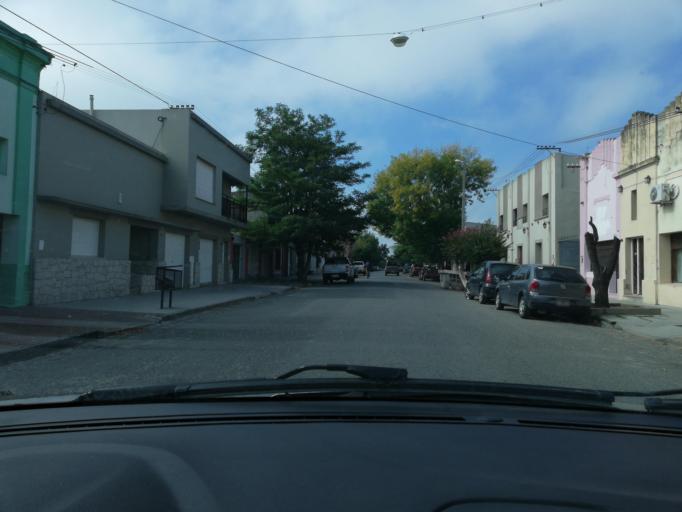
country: AR
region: Buenos Aires
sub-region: Partido de Balcarce
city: Balcarce
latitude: -37.8411
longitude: -58.2583
